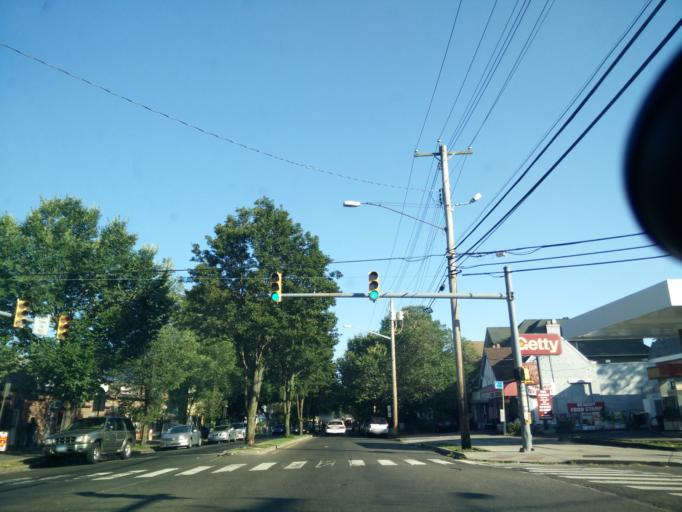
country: US
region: Connecticut
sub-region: Fairfield County
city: Bridgeport
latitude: 41.1778
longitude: -73.2013
